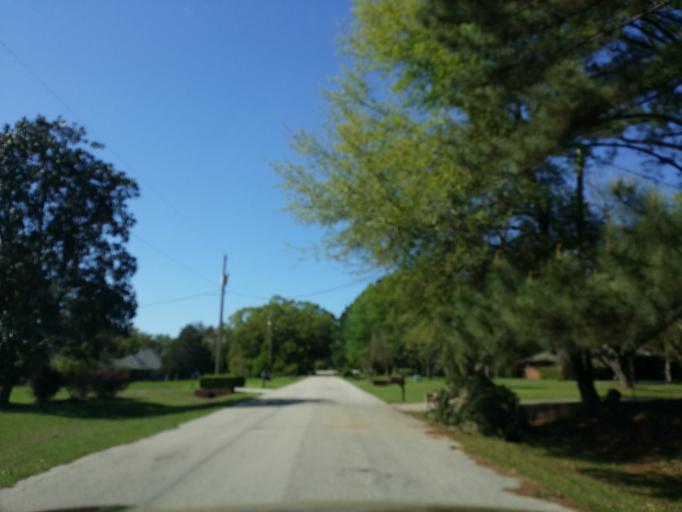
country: US
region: Florida
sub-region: Leon County
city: Tallahassee
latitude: 30.4816
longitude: -84.1853
